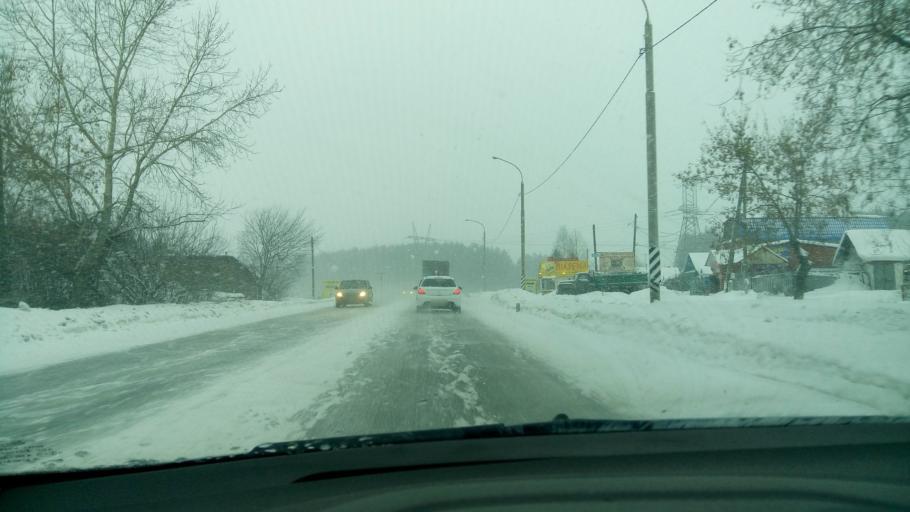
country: RU
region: Sverdlovsk
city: Beloyarskiy
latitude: 56.7698
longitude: 61.4342
